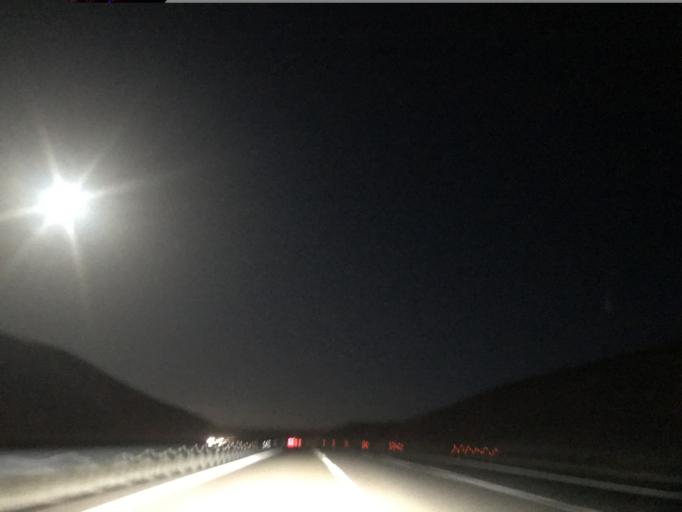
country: TR
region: Nigde
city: Ulukisla
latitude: 37.6420
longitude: 34.3790
